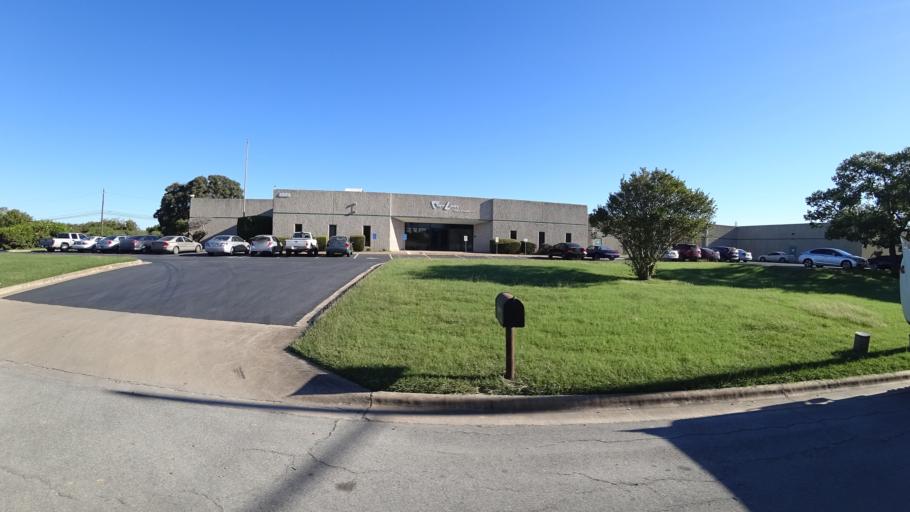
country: US
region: Texas
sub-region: Travis County
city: Manor
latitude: 30.3238
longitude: -97.6552
